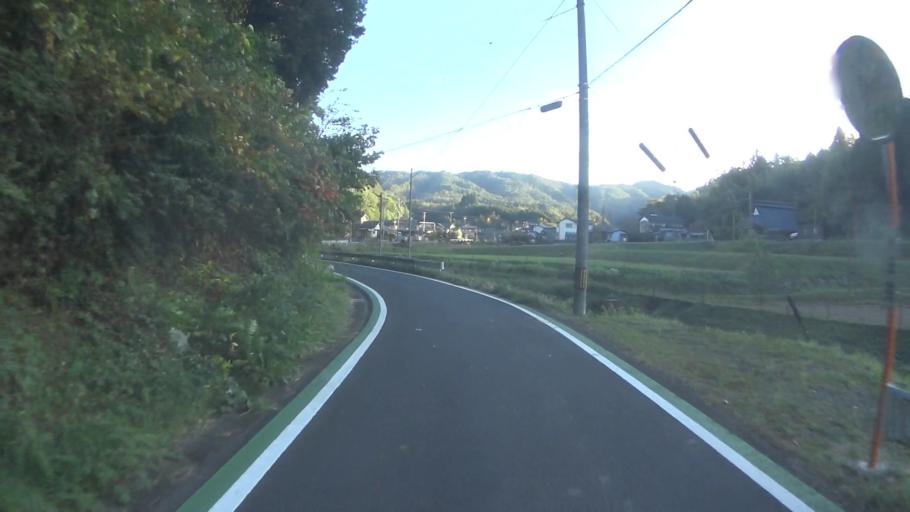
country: JP
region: Kyoto
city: Ayabe
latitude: 35.2847
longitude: 135.2498
